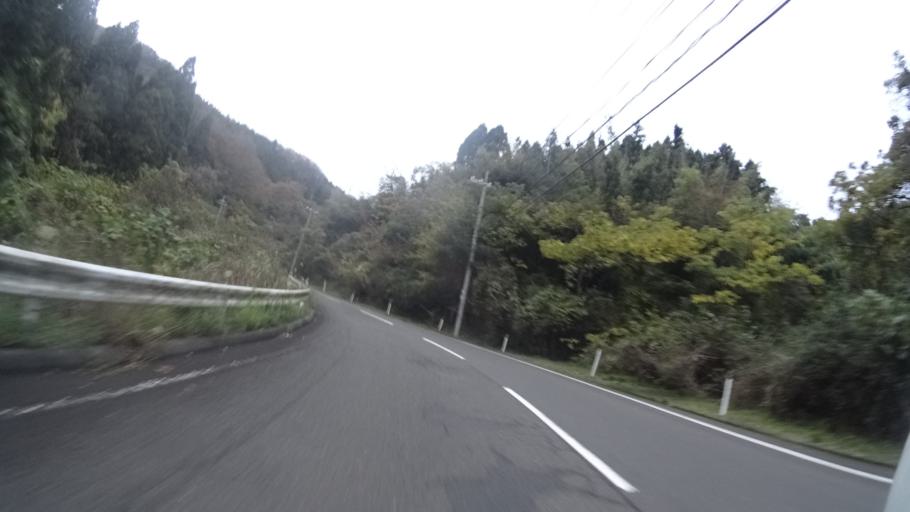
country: JP
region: Kyoto
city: Maizuru
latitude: 35.5546
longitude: 135.4544
